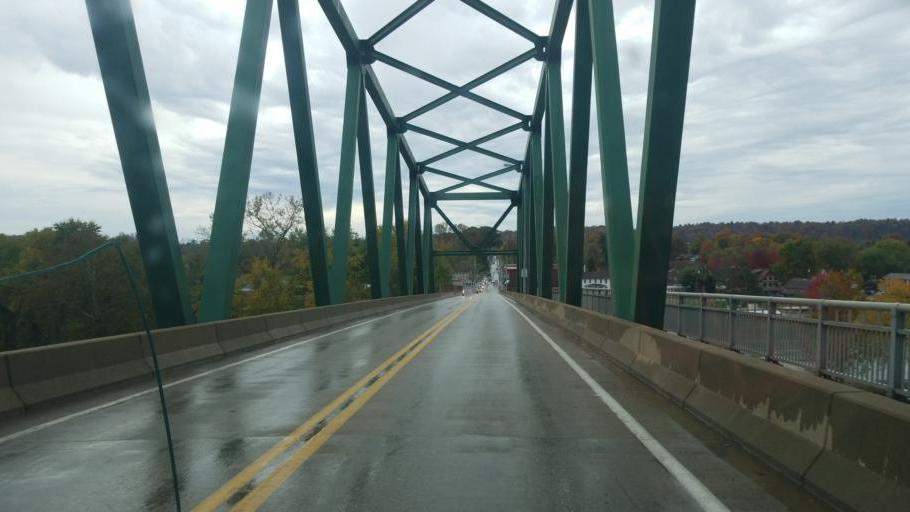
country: US
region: West Virginia
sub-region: Wood County
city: Williamstown
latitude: 39.4081
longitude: -81.4482
